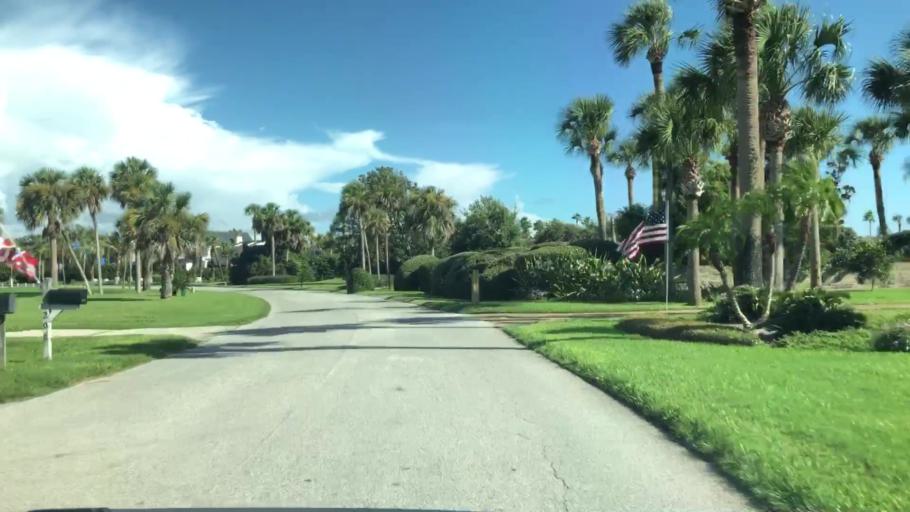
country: US
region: Florida
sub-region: Saint Johns County
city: Ponte Vedra Beach
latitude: 30.2414
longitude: -81.3816
